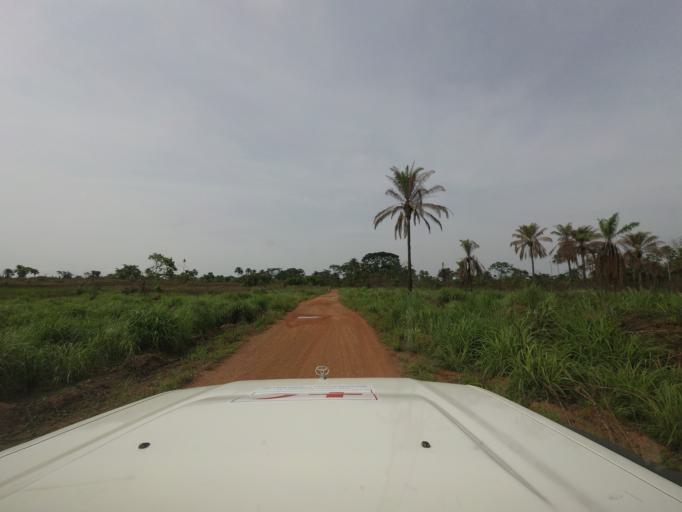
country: GN
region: Nzerekore
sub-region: Macenta
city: Macenta
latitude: 8.5029
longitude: -9.5310
